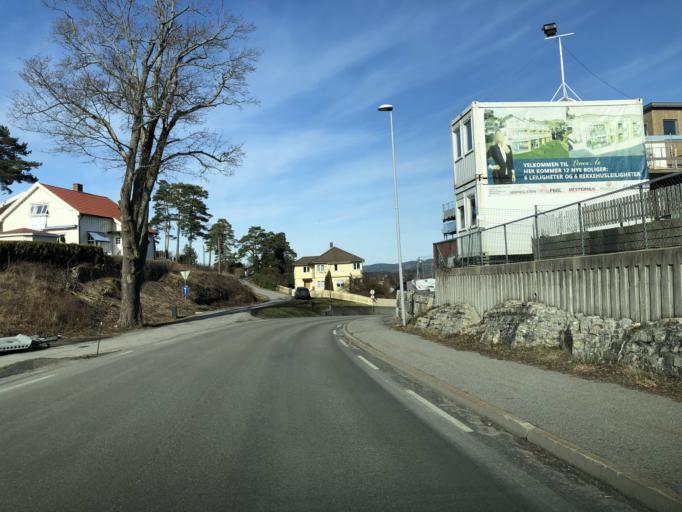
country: NO
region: Telemark
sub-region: Bamble
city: Langesund
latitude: 59.0065
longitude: 9.7441
